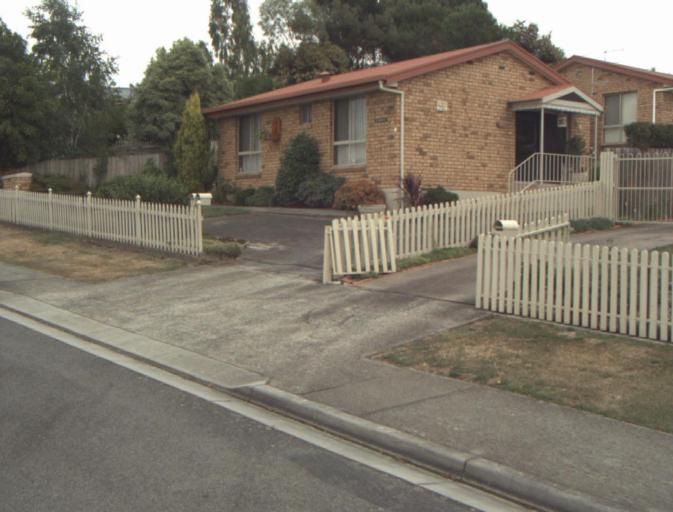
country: AU
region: Tasmania
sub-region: Launceston
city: Summerhill
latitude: -41.4839
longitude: 147.1670
